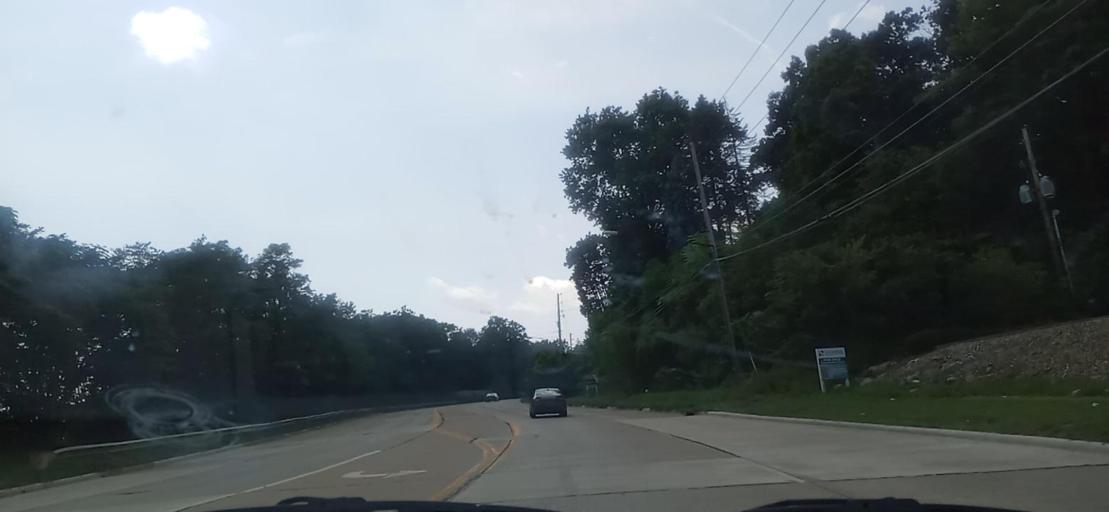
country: US
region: Ohio
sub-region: Summit County
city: Barberton
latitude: 41.0624
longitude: -81.5783
